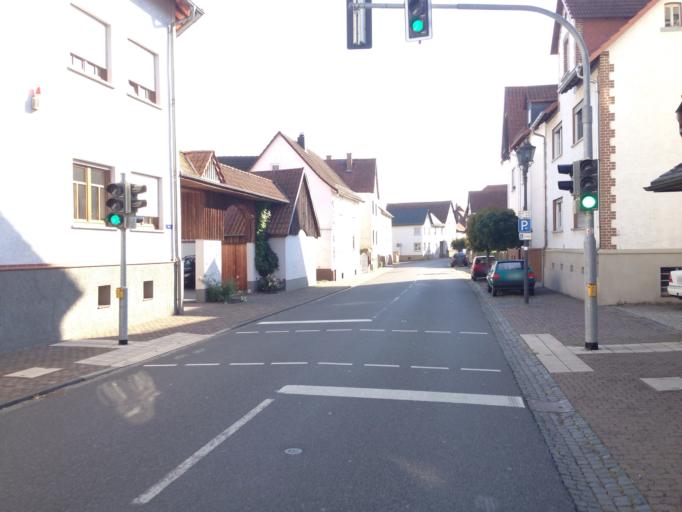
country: DE
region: Hesse
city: Lollar
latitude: 50.6376
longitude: 8.6765
